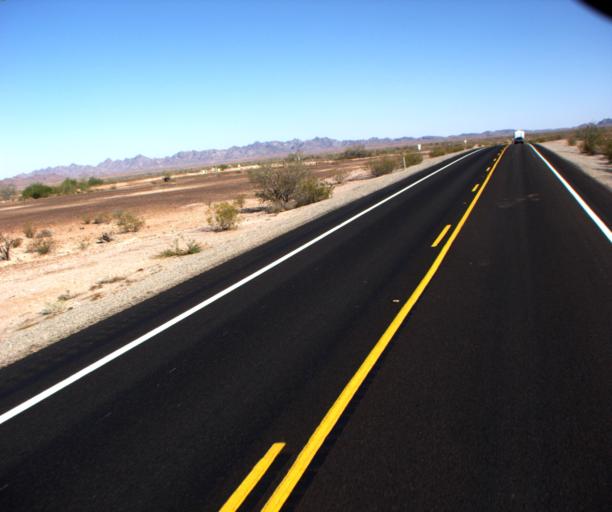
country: US
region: Arizona
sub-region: Yuma County
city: Wellton
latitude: 33.1167
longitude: -114.2934
